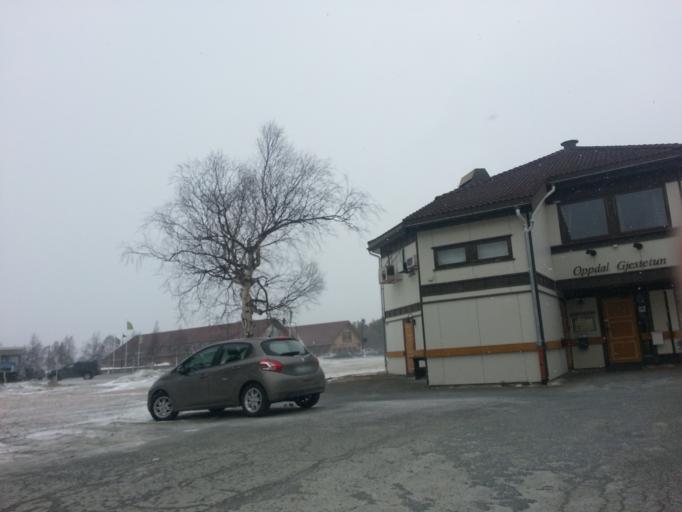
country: NO
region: Sor-Trondelag
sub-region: Oppdal
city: Oppdal
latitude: 62.5921
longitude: 9.6876
